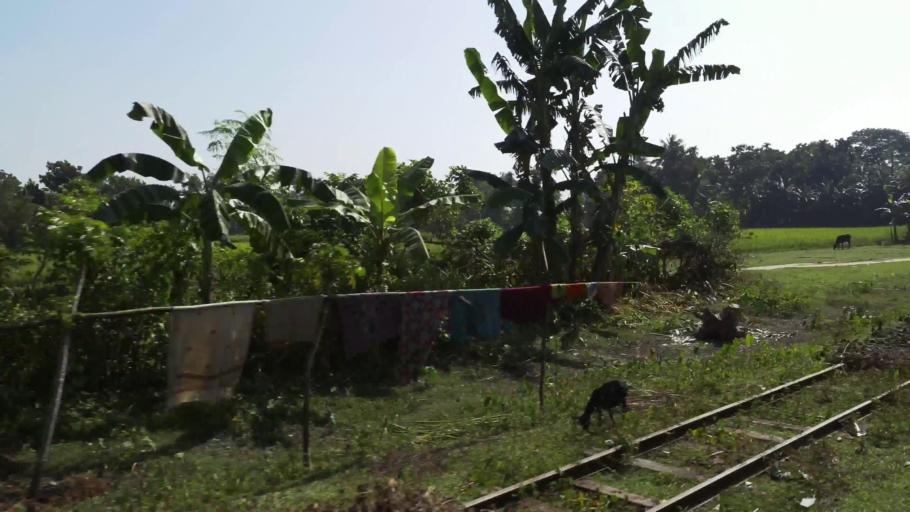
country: BD
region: Dhaka
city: Gafargaon
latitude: 24.5862
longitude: 90.5070
